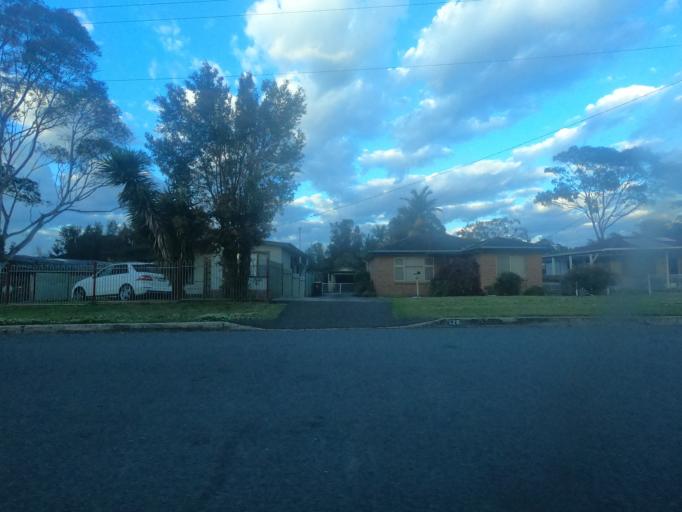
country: AU
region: New South Wales
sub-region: Wollongong
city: Koonawarra
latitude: -34.4978
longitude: 150.8138
